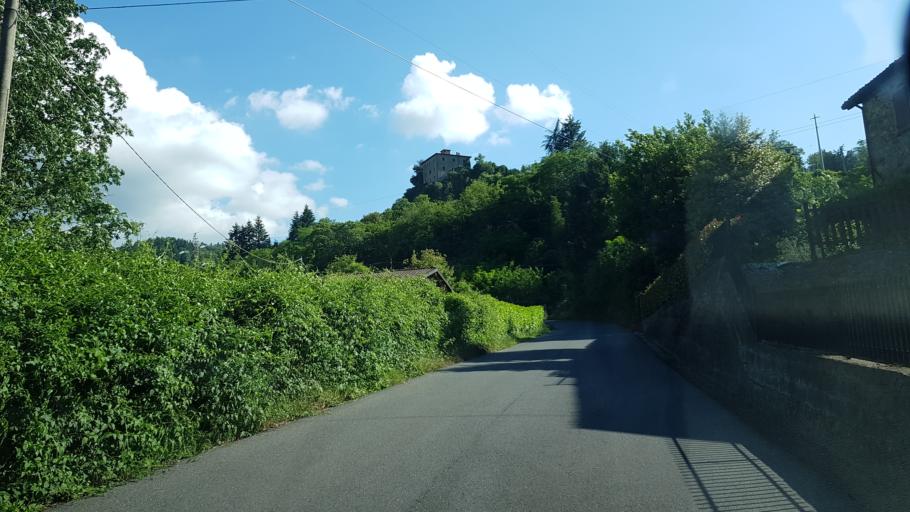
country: IT
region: Tuscany
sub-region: Provincia di Lucca
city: Camporgiano
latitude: 44.1611
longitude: 10.3376
